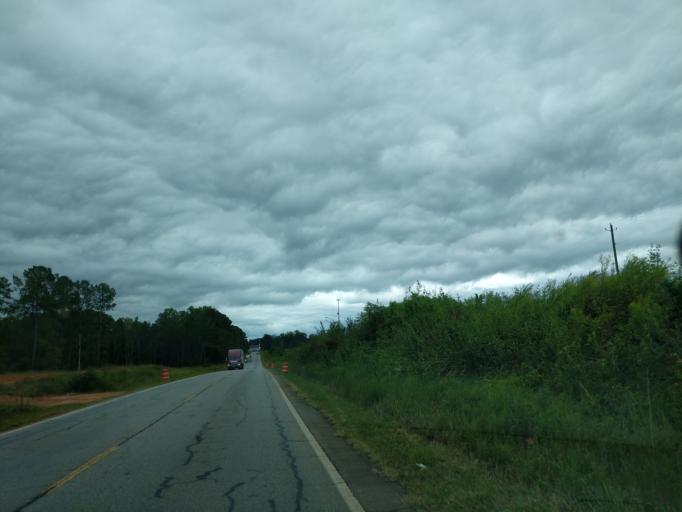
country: US
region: Georgia
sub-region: Wilkes County
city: Washington
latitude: 33.6795
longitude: -82.6306
